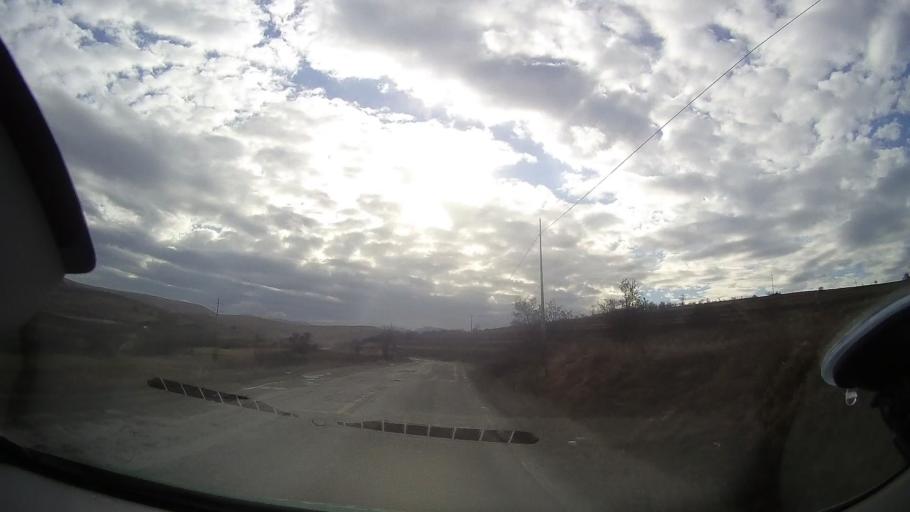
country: RO
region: Cluj
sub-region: Comuna Baisoara
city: Baisoara
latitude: 46.6061
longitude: 23.4592
